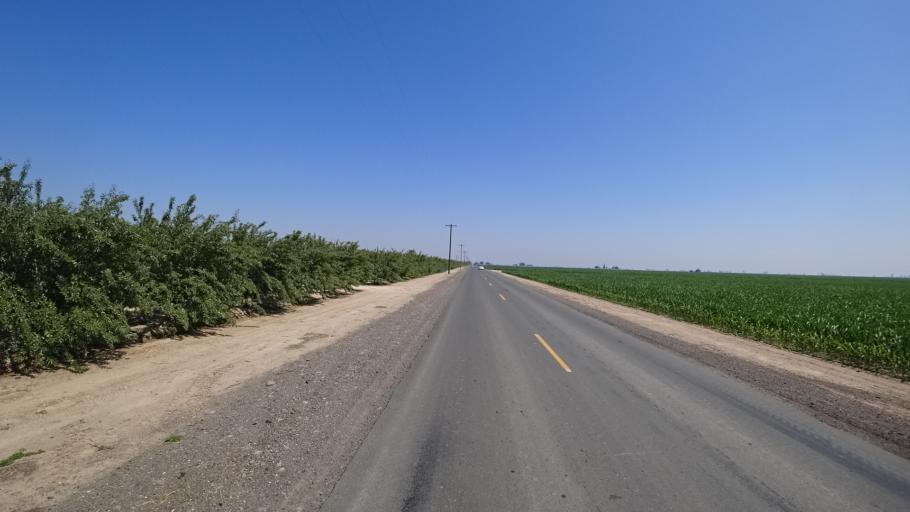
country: US
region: California
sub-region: Fresno County
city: Kingsburg
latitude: 36.4341
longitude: -119.5287
